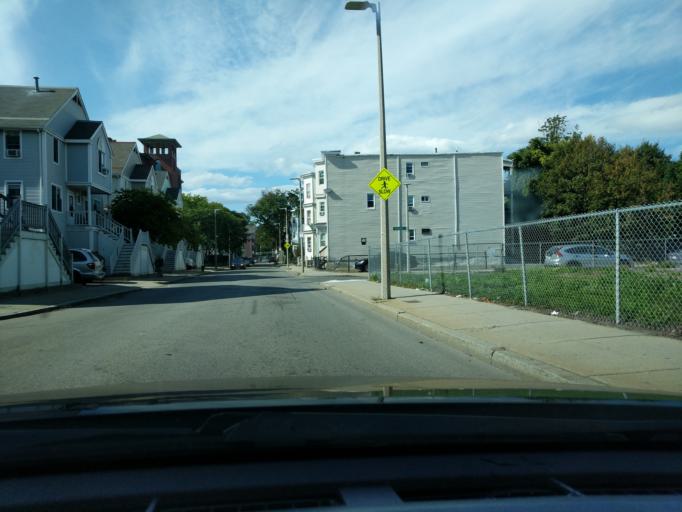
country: US
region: Massachusetts
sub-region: Suffolk County
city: South Boston
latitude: 42.3131
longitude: -71.0753
